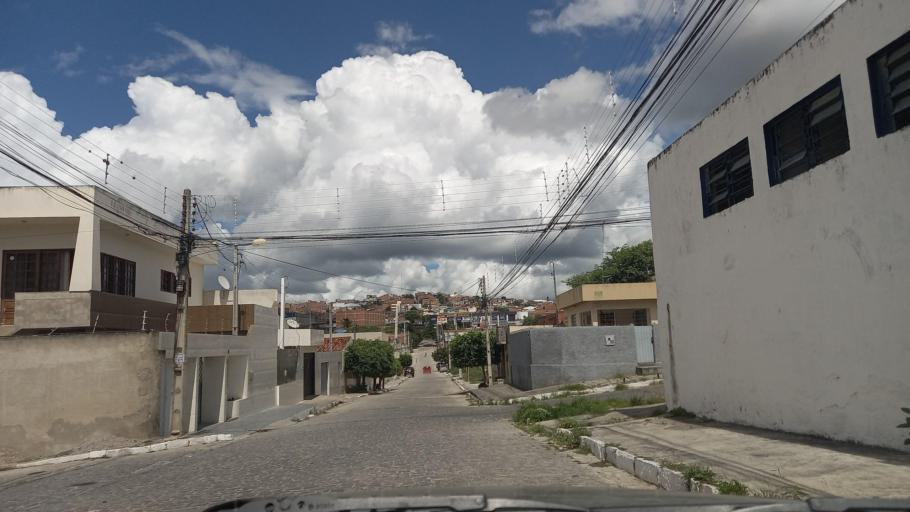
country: BR
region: Pernambuco
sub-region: Caruaru
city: Caruaru
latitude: -8.3003
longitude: -35.9758
